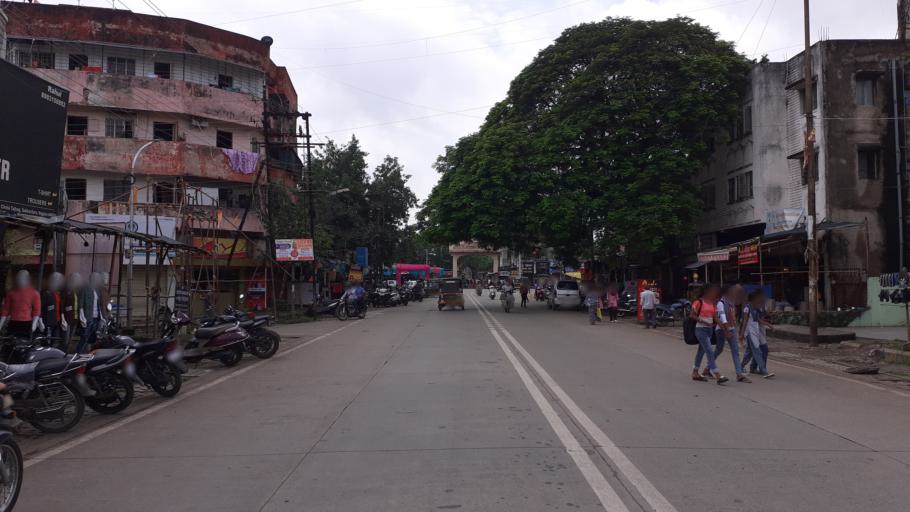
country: IN
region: Maharashtra
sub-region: Nagpur Division
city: Nagpur
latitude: 21.1243
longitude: 79.1128
